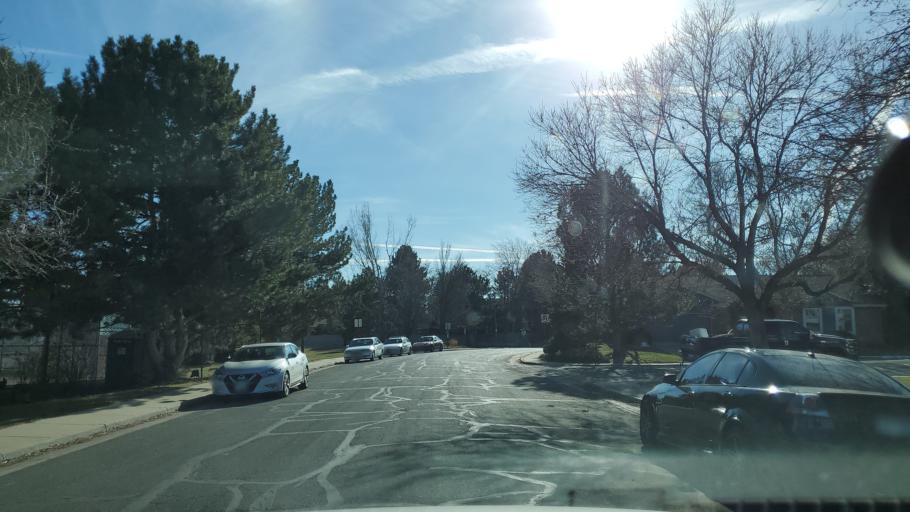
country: US
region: Colorado
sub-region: Adams County
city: Northglenn
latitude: 39.9220
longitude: -104.9523
